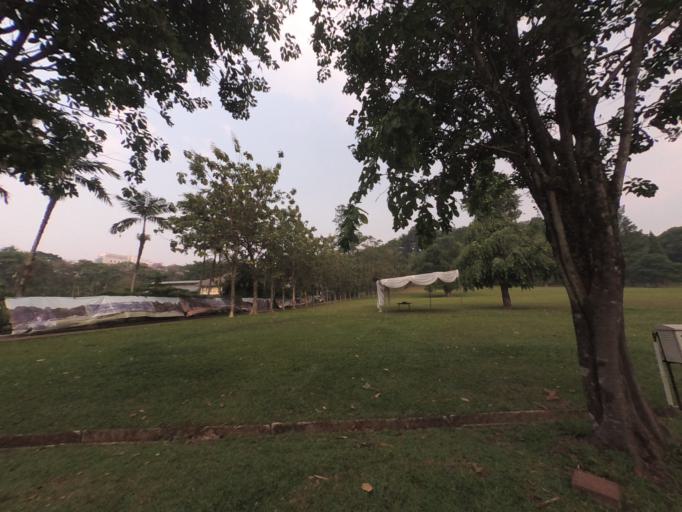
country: ID
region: West Java
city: Bogor
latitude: -6.5959
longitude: 106.8024
